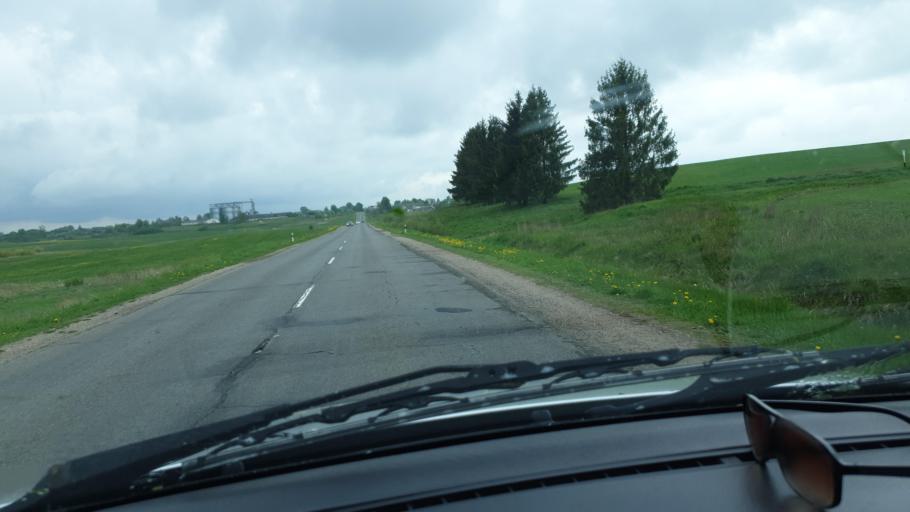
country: BY
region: Vitebsk
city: Lyepyel'
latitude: 54.8843
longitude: 28.6444
